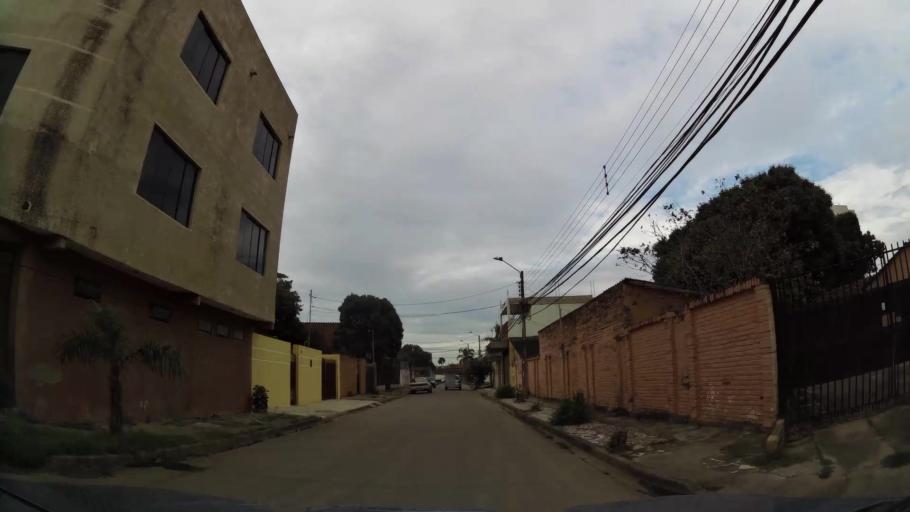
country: BO
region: Santa Cruz
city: Santa Cruz de la Sierra
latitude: -17.7667
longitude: -63.1645
